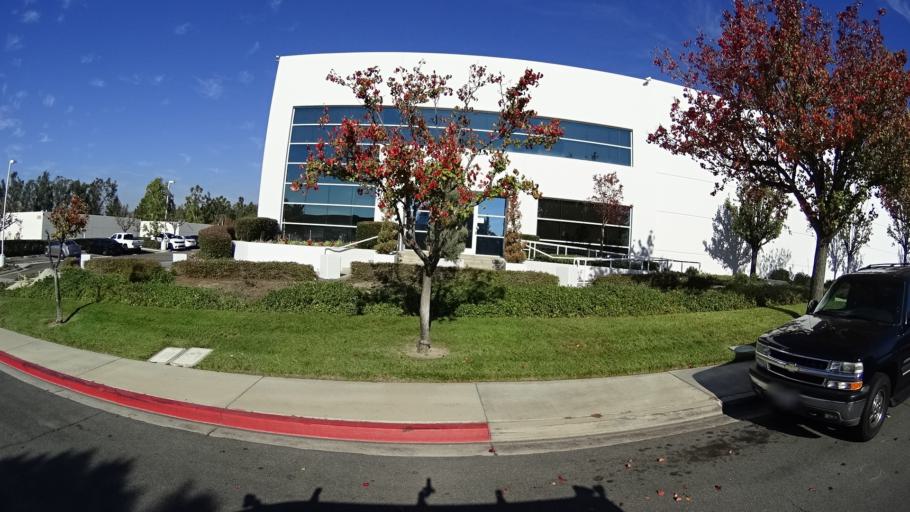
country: US
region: California
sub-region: Orange County
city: Foothill Ranch
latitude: 33.6657
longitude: -117.6620
